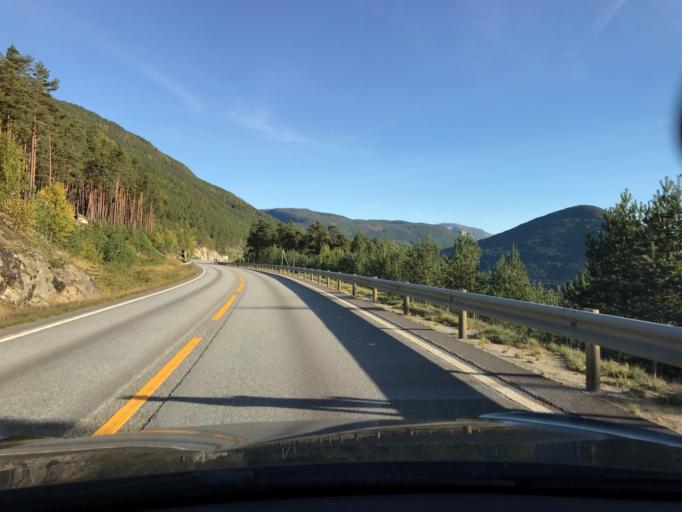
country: NO
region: Sogn og Fjordane
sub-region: Sogndal
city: Sogndalsfjora
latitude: 61.1884
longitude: 7.2302
